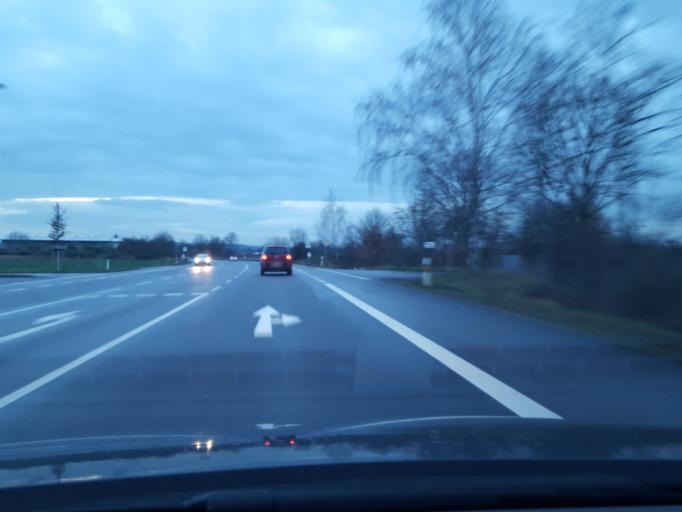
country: DE
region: North Rhine-Westphalia
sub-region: Regierungsbezirk Koln
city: Bonn
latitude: 50.7838
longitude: 7.0910
